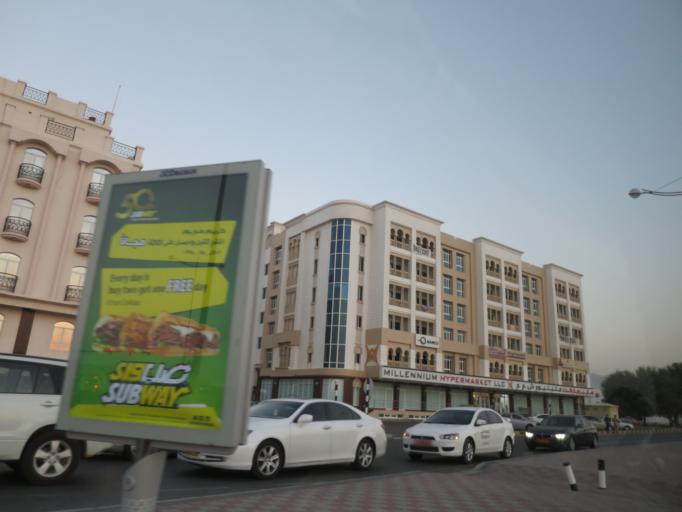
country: OM
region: Muhafazat Masqat
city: Bawshar
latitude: 23.5986
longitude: 58.3846
